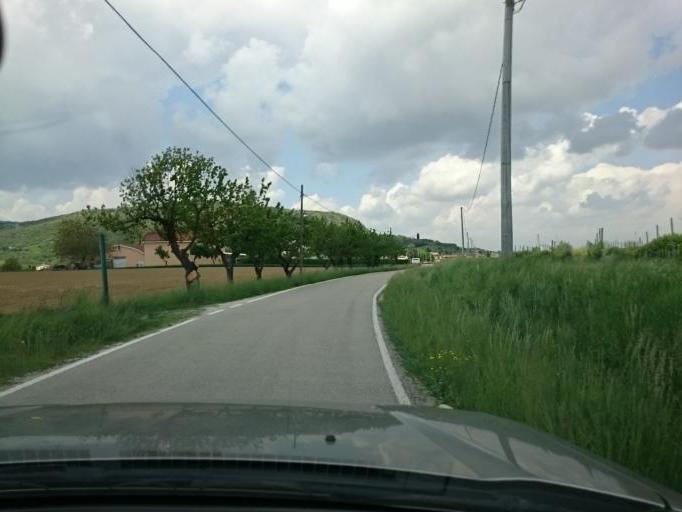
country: IT
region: Veneto
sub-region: Provincia di Vicenza
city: Longare
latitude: 45.4644
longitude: 11.6184
